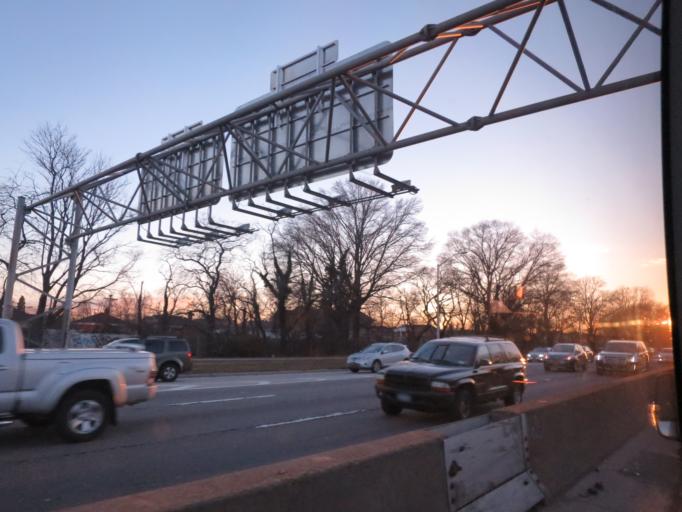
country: US
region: New York
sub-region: Queens County
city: Borough of Queens
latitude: 40.6647
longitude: -73.8449
